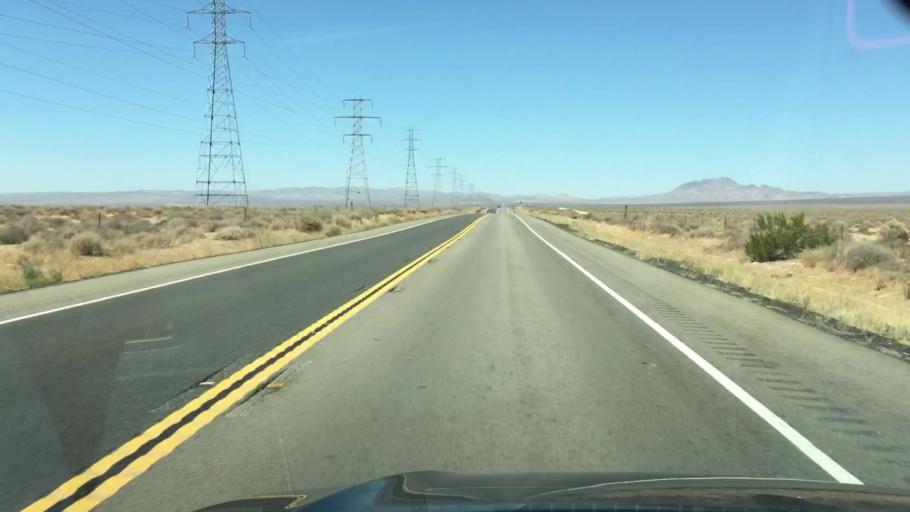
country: US
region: California
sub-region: Kern County
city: Boron
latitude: 35.1447
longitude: -117.5841
